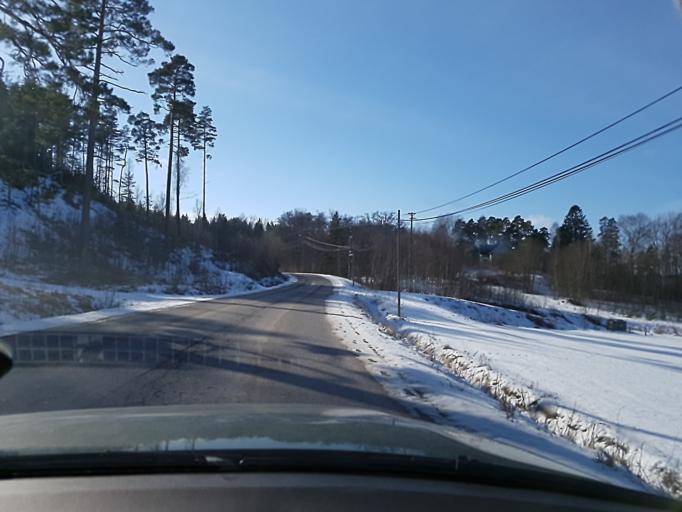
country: FI
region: Uusimaa
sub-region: Helsinki
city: Siuntio
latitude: 60.1110
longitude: 24.2988
